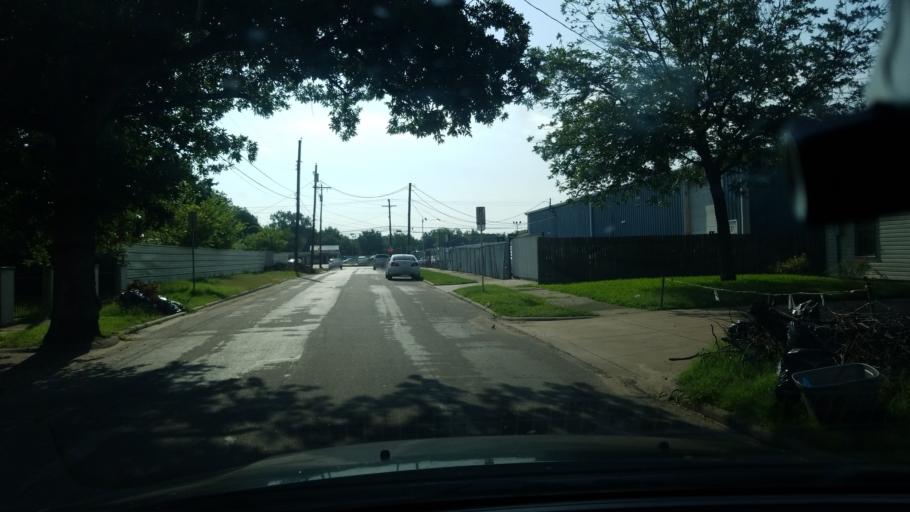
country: US
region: Texas
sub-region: Dallas County
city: Balch Springs
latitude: 32.7237
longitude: -96.6844
